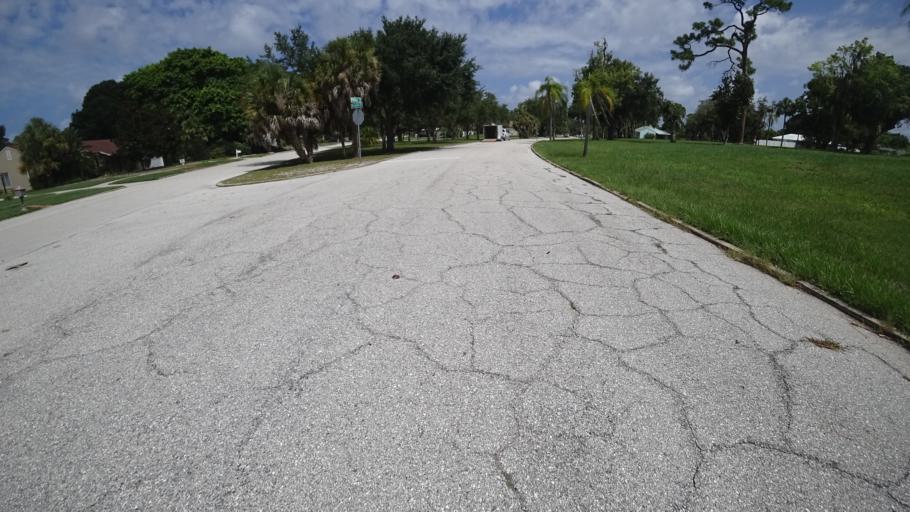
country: US
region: Florida
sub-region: Manatee County
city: Whitfield
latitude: 27.4076
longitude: -82.5722
